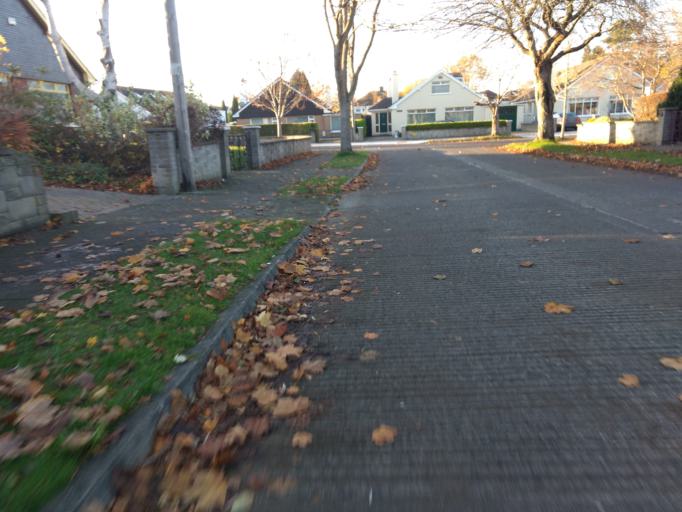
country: IE
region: Leinster
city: Malahide
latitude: 53.4504
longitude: -6.1718
